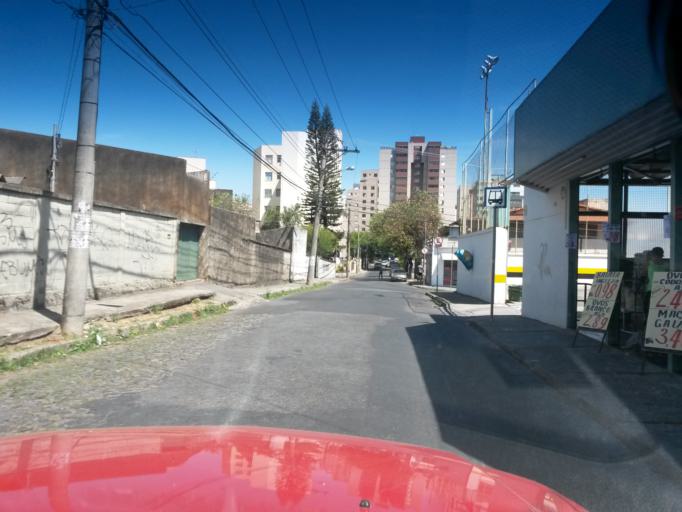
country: BR
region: Minas Gerais
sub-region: Belo Horizonte
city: Belo Horizonte
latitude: -19.9033
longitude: -43.9720
